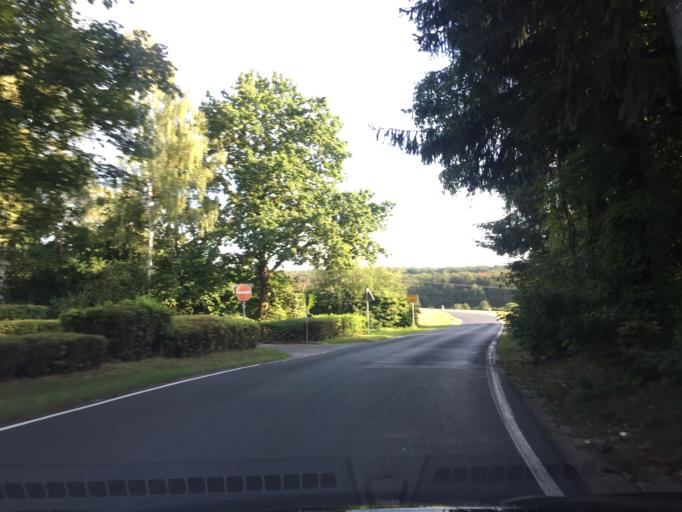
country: DE
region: Rheinland-Pfalz
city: Ruppach-Goldhausen
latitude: 50.4595
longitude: 7.8819
